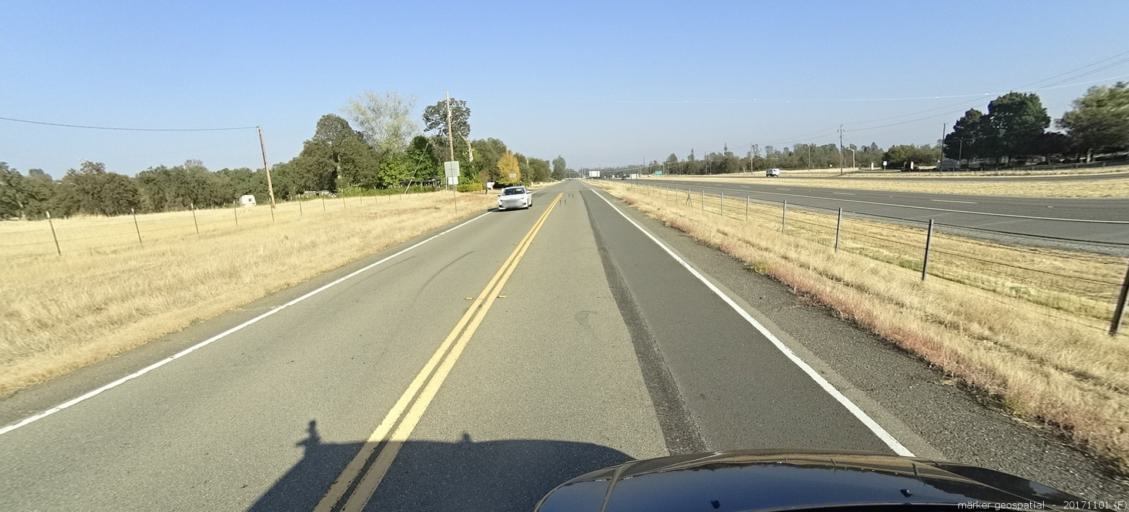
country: US
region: California
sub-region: Shasta County
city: Redding
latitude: 40.6185
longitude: -122.3310
